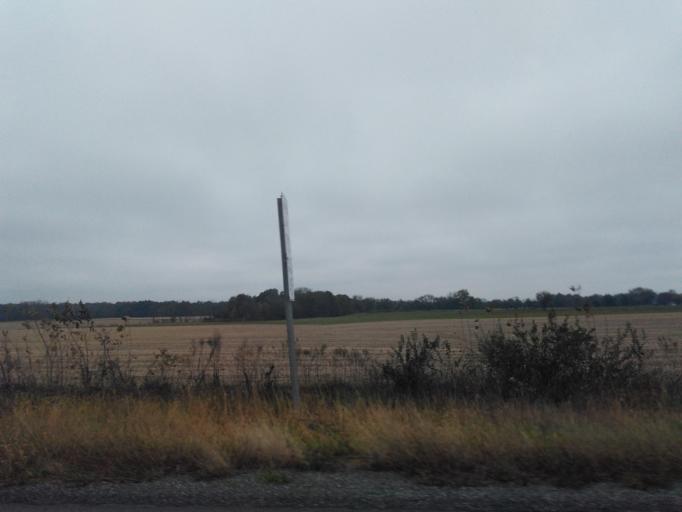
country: US
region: Illinois
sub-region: Madison County
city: Highland
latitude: 38.7867
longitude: -89.6436
